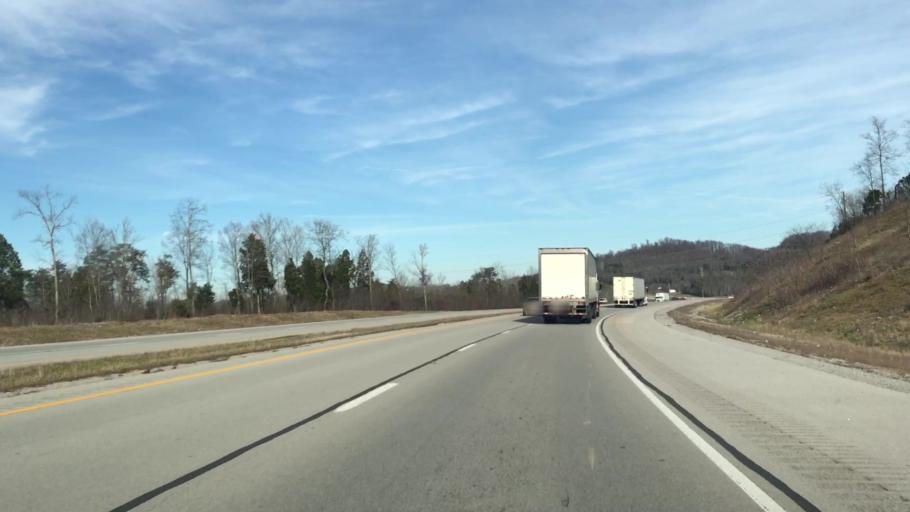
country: US
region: Kentucky
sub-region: Pulaski County
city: Somerset
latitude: 37.0158
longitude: -84.5998
